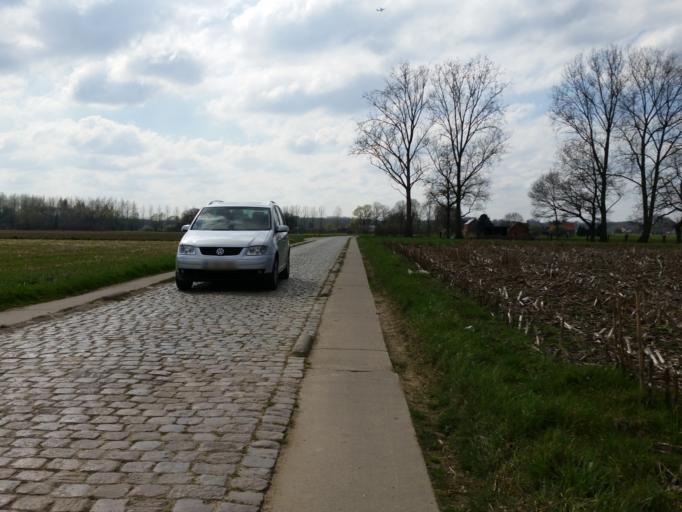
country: BE
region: Flanders
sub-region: Provincie Vlaams-Brabant
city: Haacht
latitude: 50.9355
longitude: 4.6101
